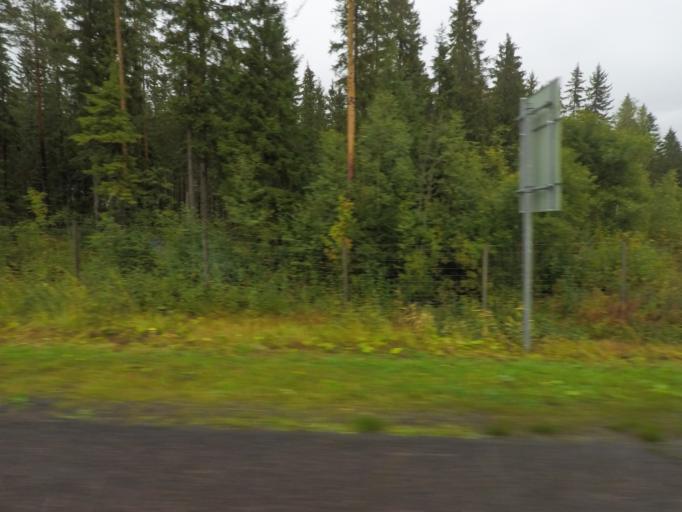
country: FI
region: Northern Savo
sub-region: Varkaus
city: Varkaus
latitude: 62.2405
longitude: 27.8884
